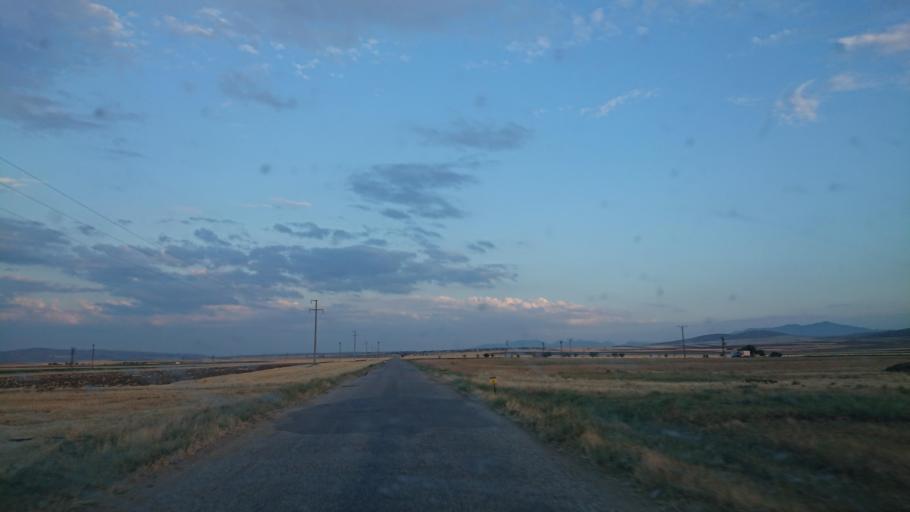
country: TR
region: Aksaray
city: Ortakoy
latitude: 38.8598
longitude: 34.0720
